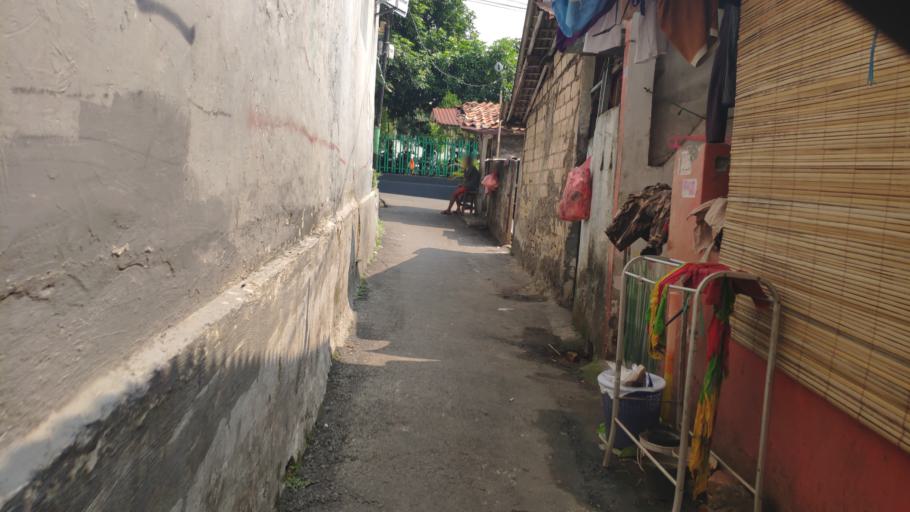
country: ID
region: Jakarta Raya
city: Jakarta
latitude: -6.2576
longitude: 106.7961
